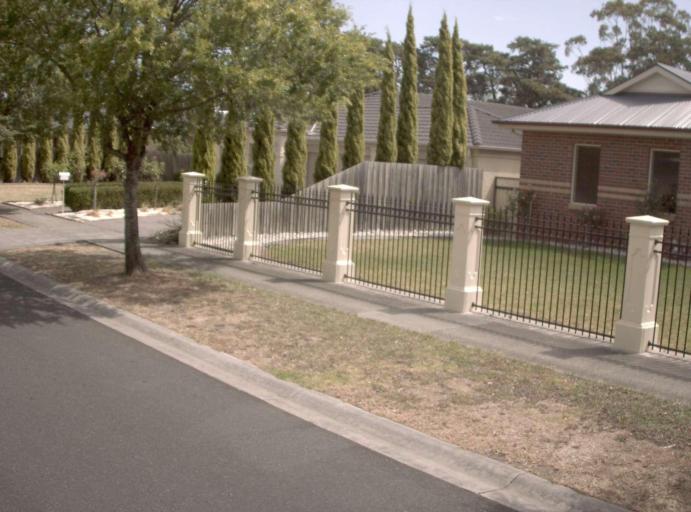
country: AU
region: Victoria
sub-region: Casey
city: Narre Warren South
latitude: -38.0309
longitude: 145.2839
